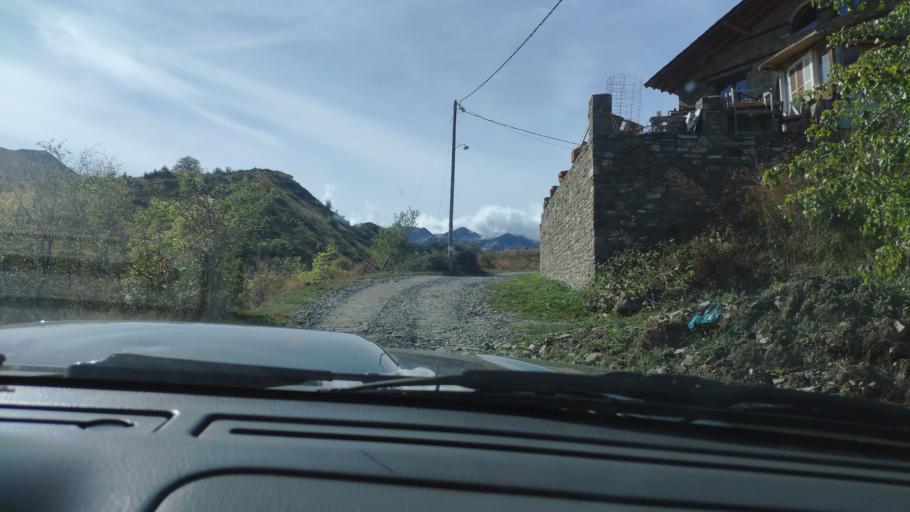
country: AL
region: Korce
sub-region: Rrethi i Devollit
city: Miras
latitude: 40.3902
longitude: 20.8352
